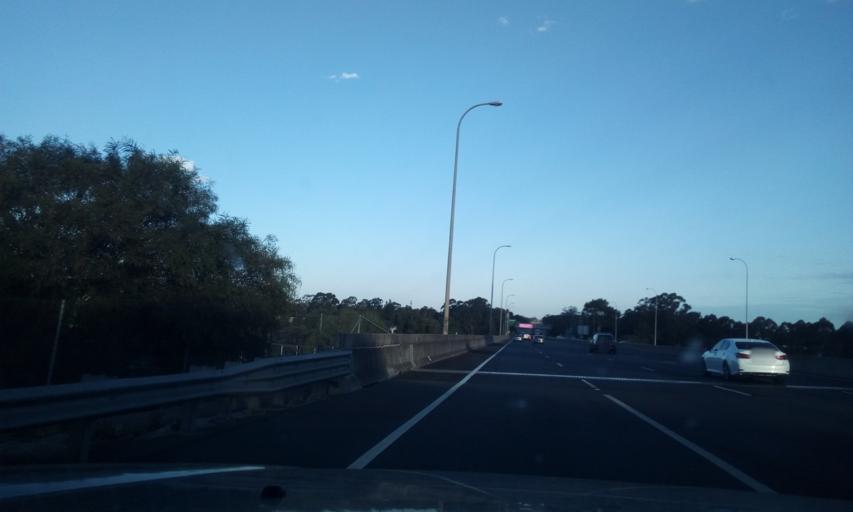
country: AU
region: New South Wales
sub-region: Campbelltown Municipality
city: Glenfield
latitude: -33.9383
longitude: 150.9181
